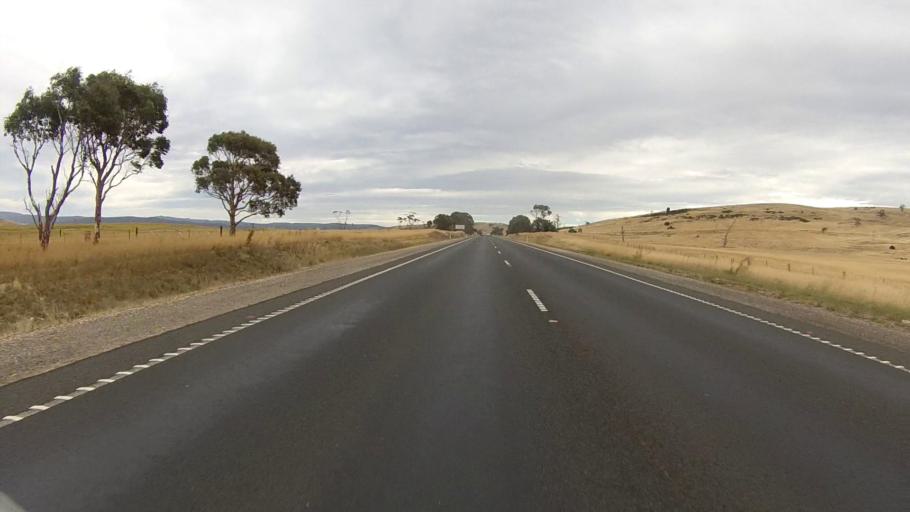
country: AU
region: Tasmania
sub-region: Brighton
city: Bridgewater
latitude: -42.3597
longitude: 147.3363
